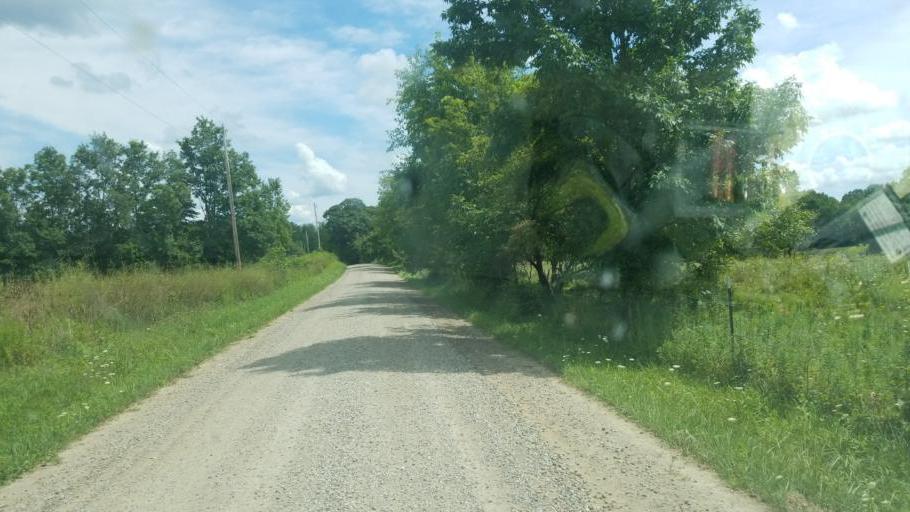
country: US
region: Ohio
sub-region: Knox County
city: Mount Vernon
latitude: 40.3706
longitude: -82.5968
